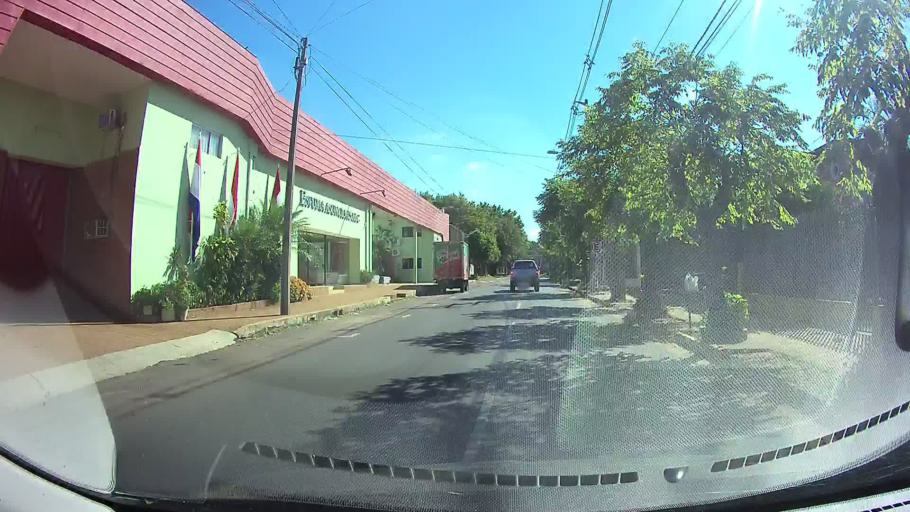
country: PY
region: Central
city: Lambare
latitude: -25.3136
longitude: -57.5691
